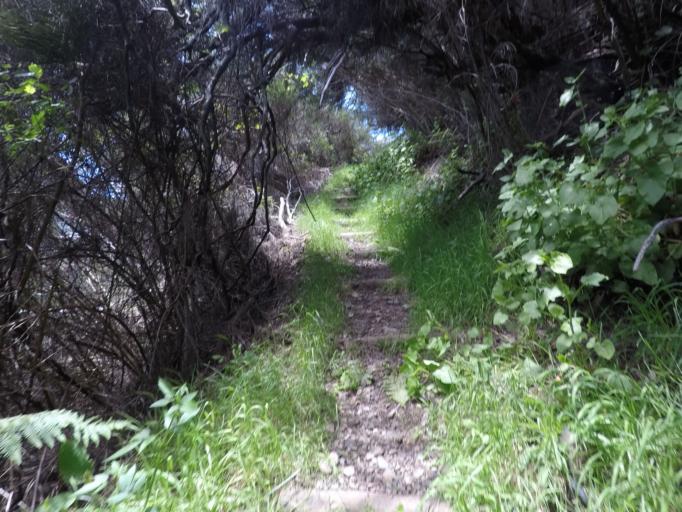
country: PT
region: Madeira
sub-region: Camara de Lobos
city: Curral das Freiras
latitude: 32.7533
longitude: -16.9722
